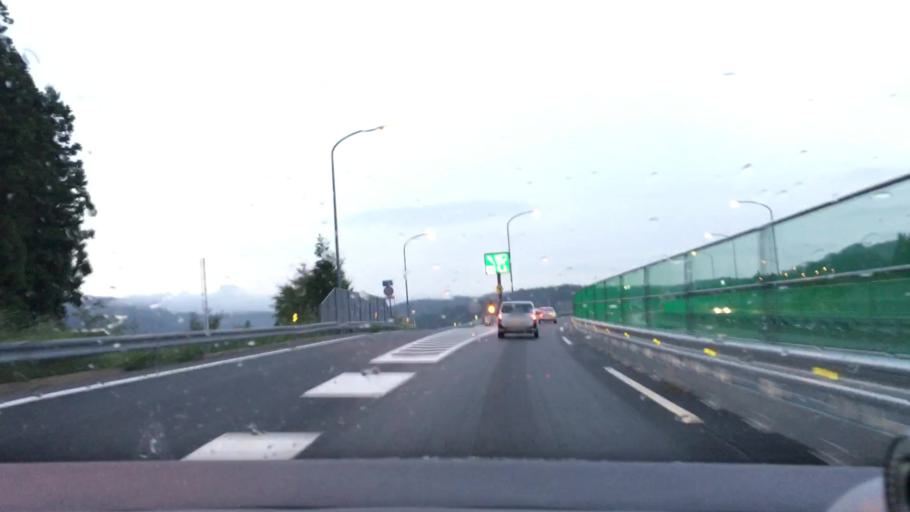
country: JP
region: Gifu
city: Gujo
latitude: 35.9347
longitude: 136.8791
